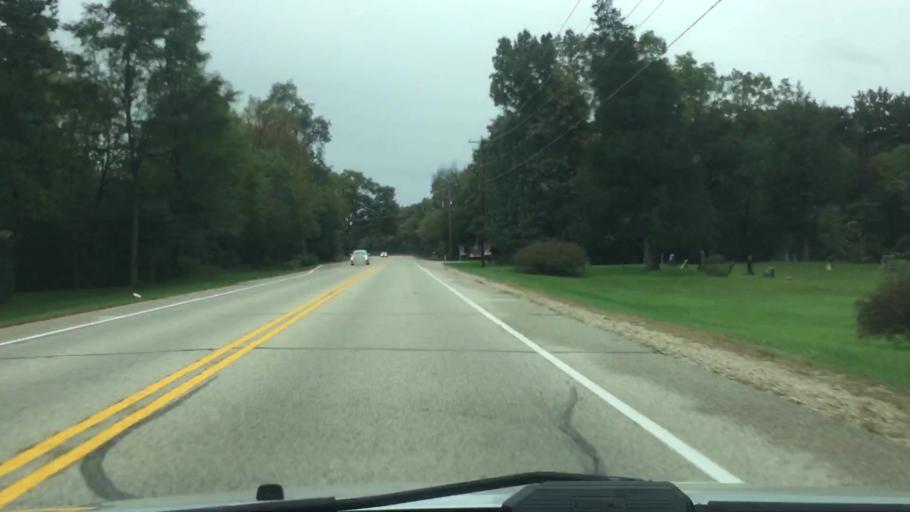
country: US
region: Wisconsin
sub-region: Waukesha County
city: Eagle
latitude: 42.8649
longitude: -88.4873
